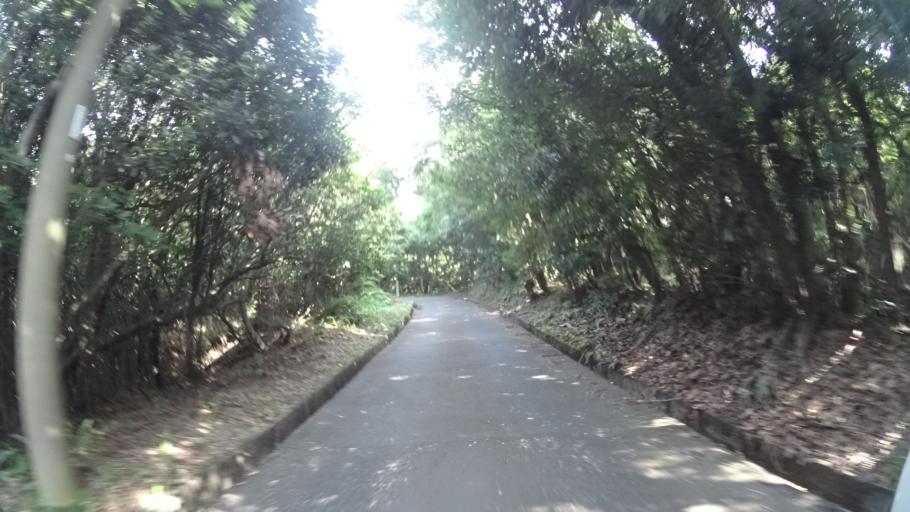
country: JP
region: Kagoshima
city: Nishinoomote
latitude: 30.3899
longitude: 130.3851
